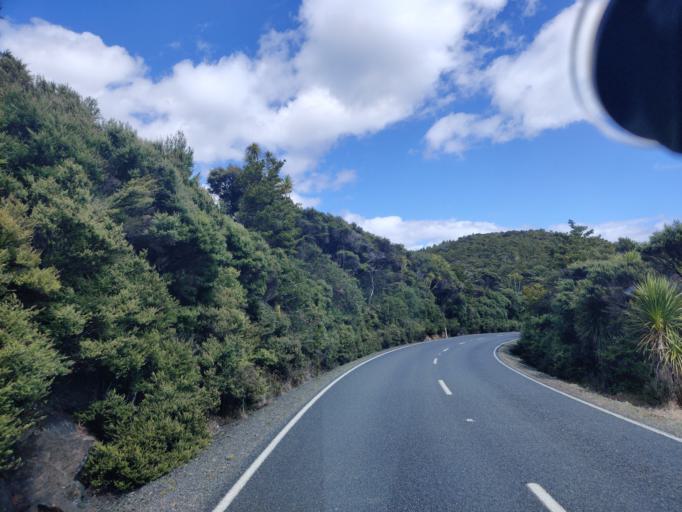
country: NZ
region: Northland
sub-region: Far North District
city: Paihia
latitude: -35.2645
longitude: 174.2633
